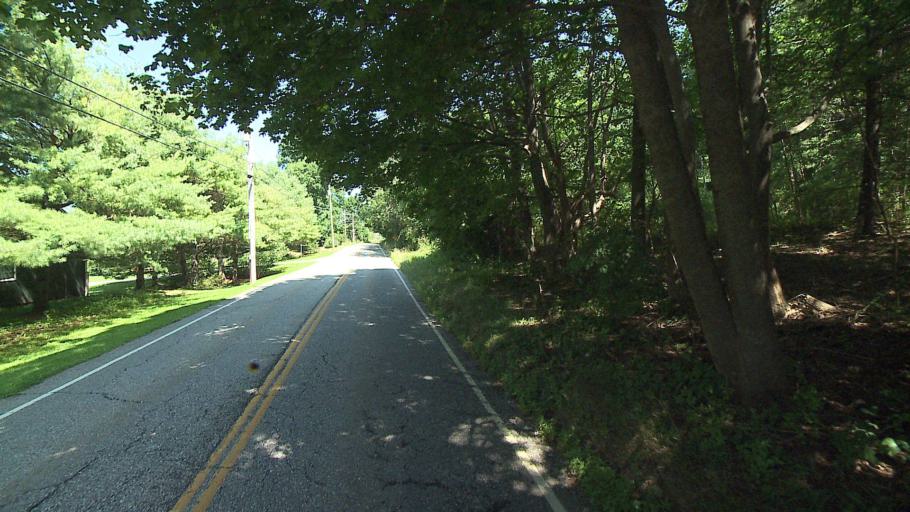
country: US
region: New York
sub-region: Dutchess County
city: Pine Plains
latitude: 41.9054
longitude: -73.4917
